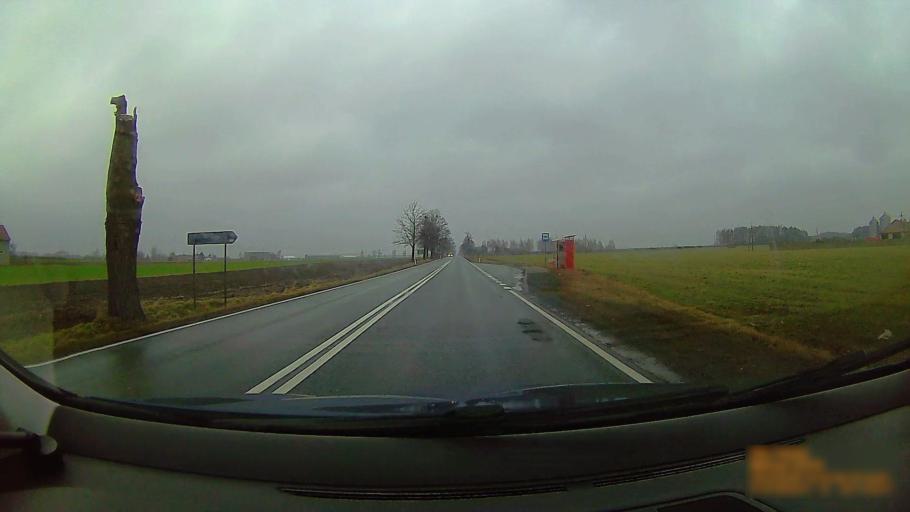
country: PL
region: Greater Poland Voivodeship
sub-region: Powiat koninski
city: Stare Miasto
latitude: 52.1396
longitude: 18.1891
